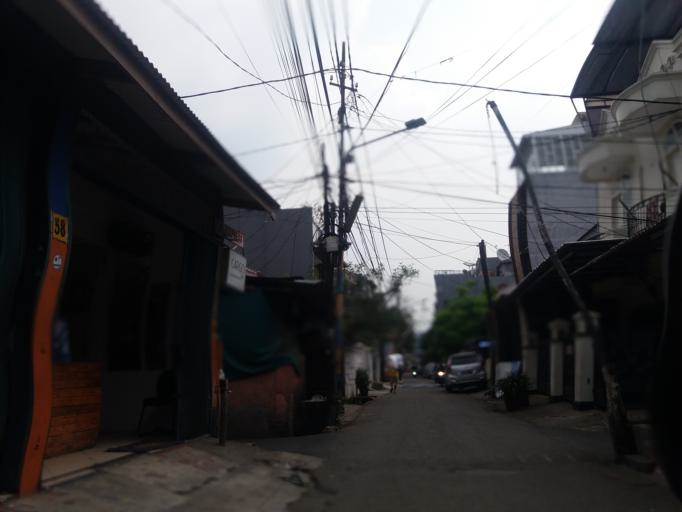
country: ID
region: Jakarta Raya
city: Jakarta
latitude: -6.1902
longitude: 106.8176
